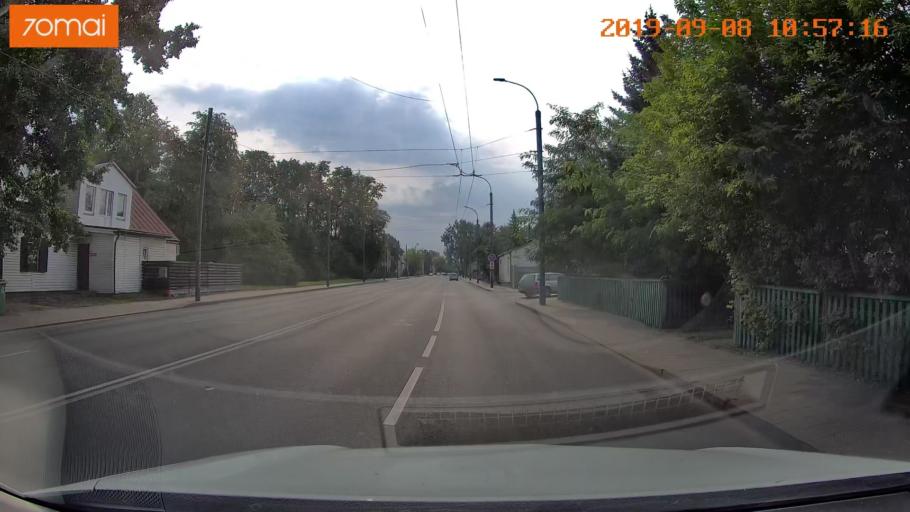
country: LT
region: Kauno apskritis
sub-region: Kaunas
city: Eiguliai
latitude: 54.9110
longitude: 23.9256
